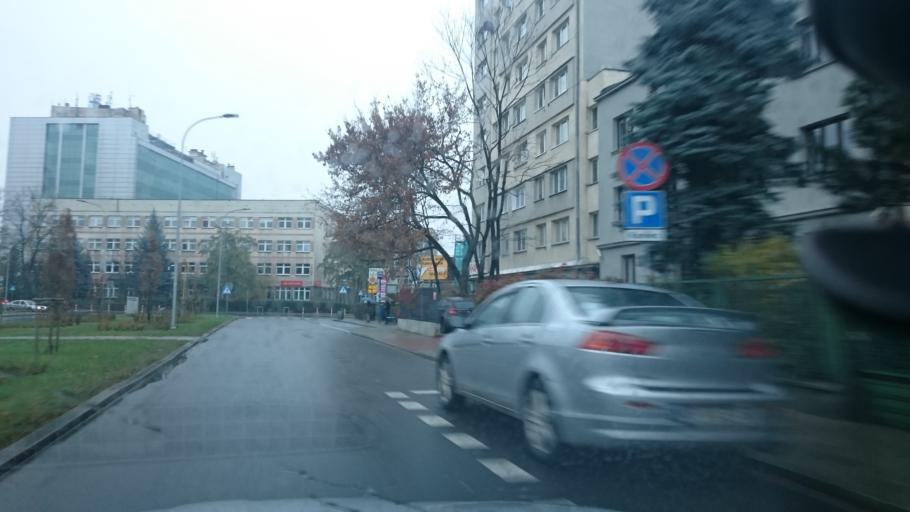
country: PL
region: Lesser Poland Voivodeship
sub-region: Krakow
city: Krakow
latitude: 50.0732
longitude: 19.9589
